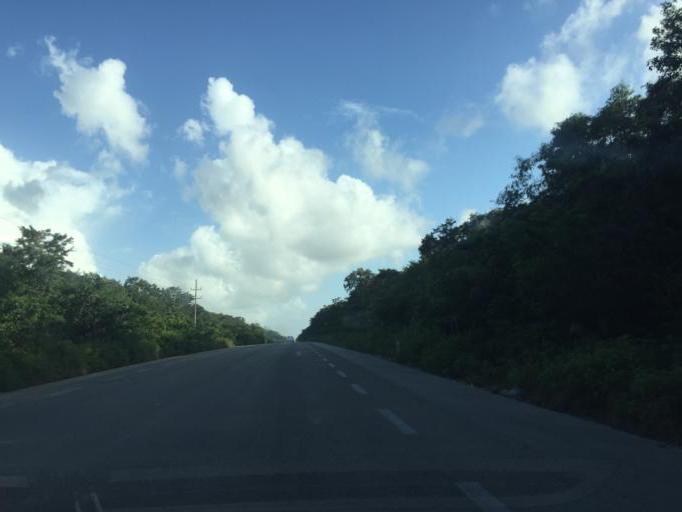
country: MX
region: Quintana Roo
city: Coba
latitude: 20.4829
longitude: -87.6970
